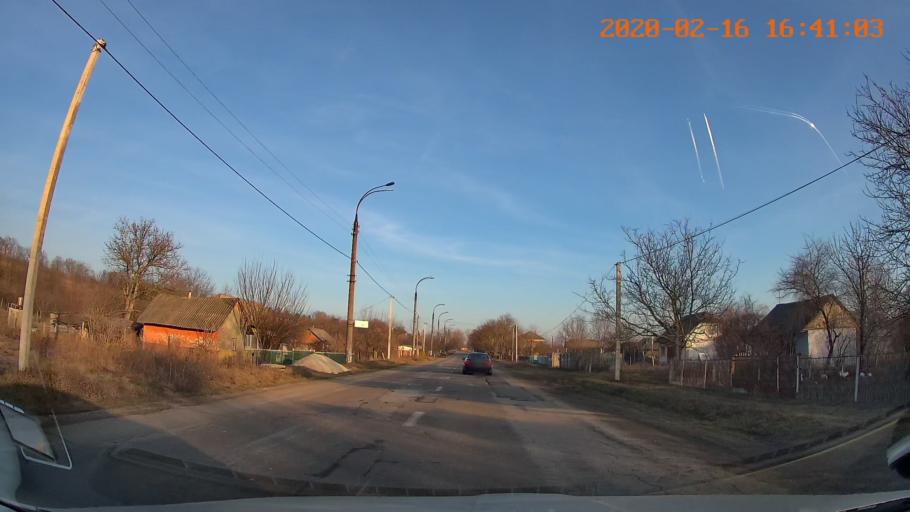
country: RO
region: Botosani
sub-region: Comuna Radauti-Prut
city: Rediu
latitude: 48.2661
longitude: 26.7738
